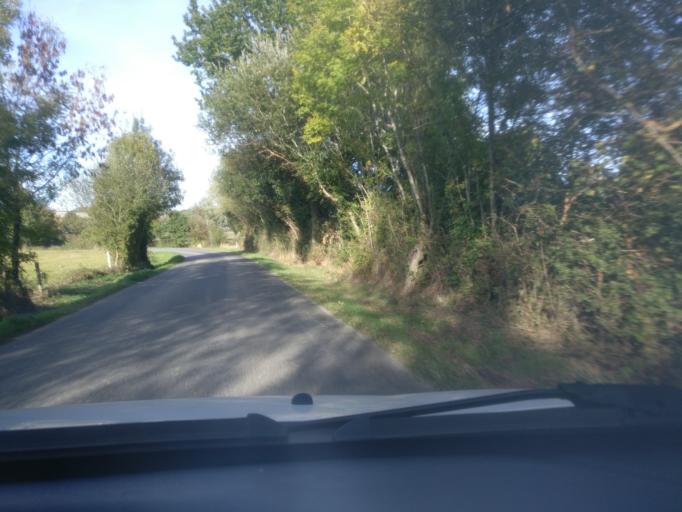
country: FR
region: Lower Normandy
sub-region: Departement de la Manche
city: Marcey-les-Greves
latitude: 48.7003
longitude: -1.4003
